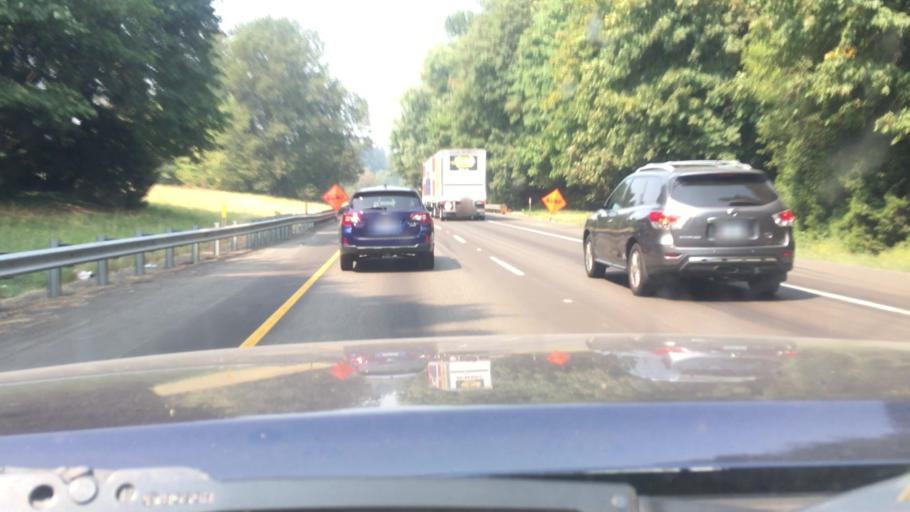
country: US
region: Oregon
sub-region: Clackamas County
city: Stafford
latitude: 45.3666
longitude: -122.6845
